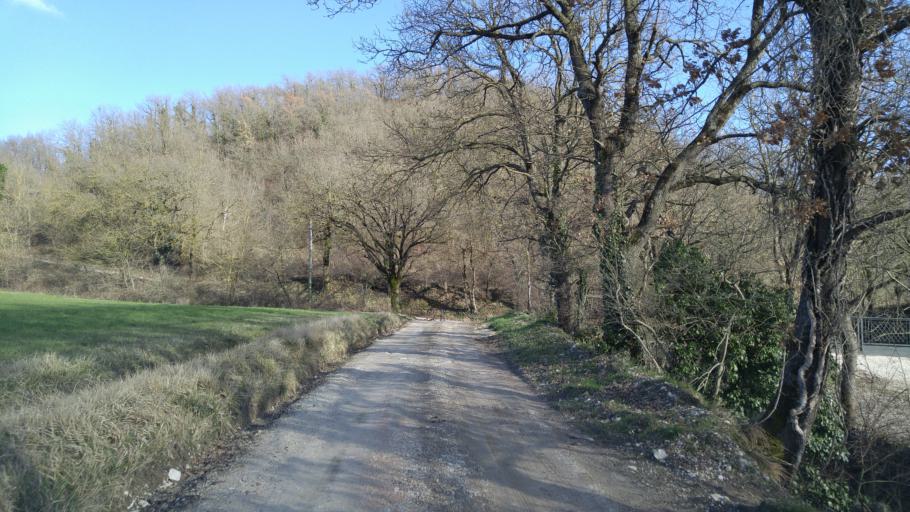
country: IT
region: The Marches
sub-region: Provincia di Pesaro e Urbino
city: Cagli
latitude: 43.5559
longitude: 12.6582
